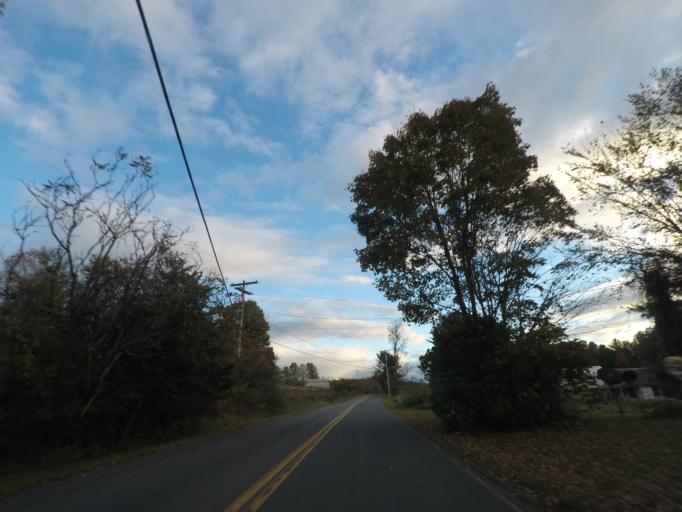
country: US
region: New York
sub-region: Rensselaer County
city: Nassau
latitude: 42.5471
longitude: -73.5876
